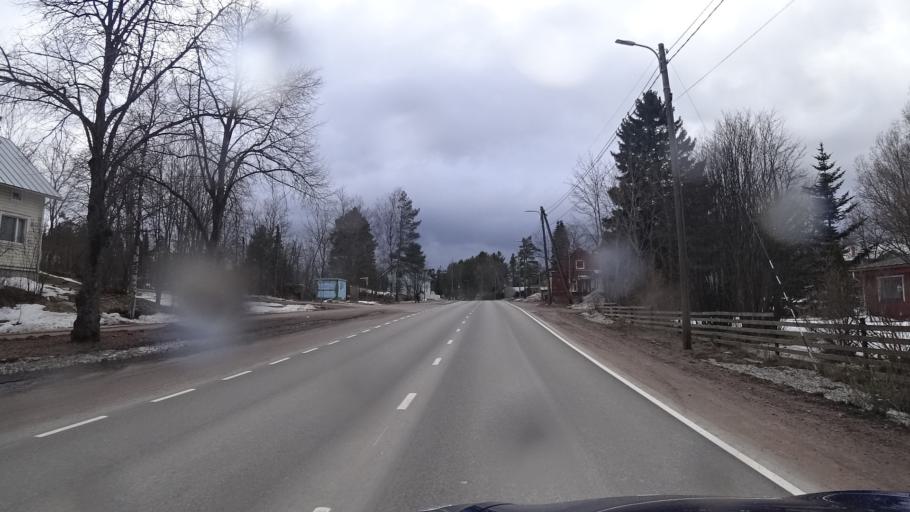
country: FI
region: Kymenlaakso
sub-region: Kotka-Hamina
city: Karhula
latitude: 60.5303
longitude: 26.9058
